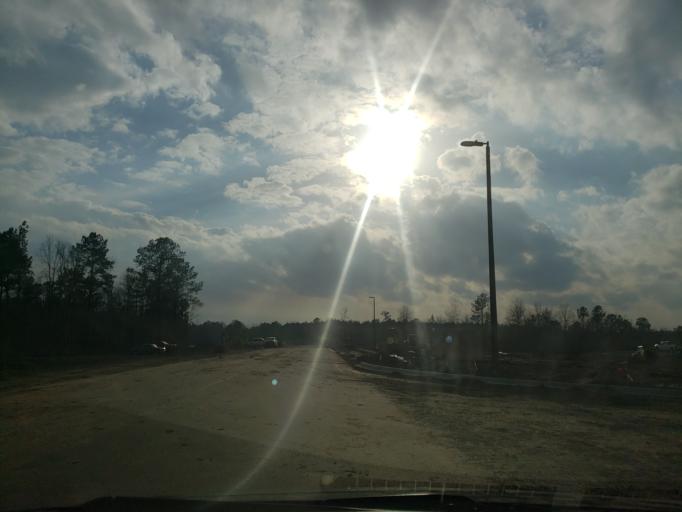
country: US
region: Georgia
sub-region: Effingham County
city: Rincon
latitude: 32.2299
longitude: -81.2097
